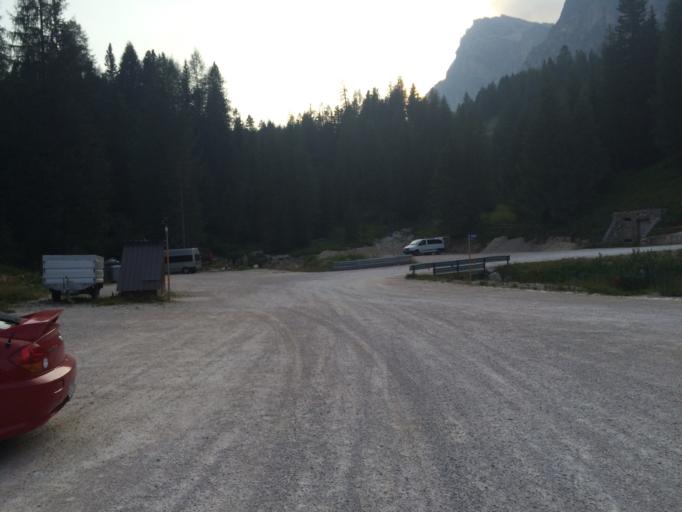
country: IT
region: Veneto
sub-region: Provincia di Belluno
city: Selva di Cadore
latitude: 46.5191
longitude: 12.0372
